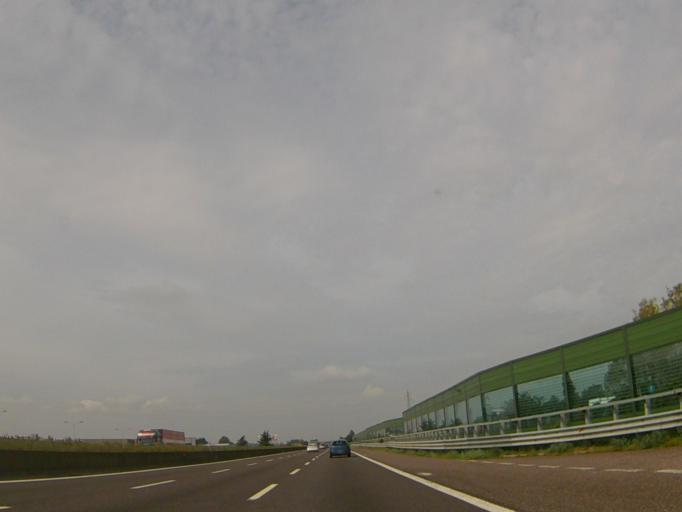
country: IT
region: Lombardy
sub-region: Provincia di Bergamo
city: Bolgare
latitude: 45.6392
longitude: 9.8305
